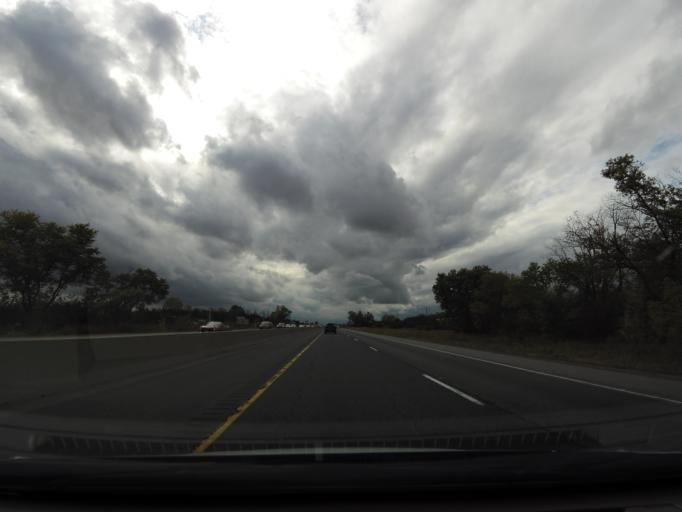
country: CA
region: Ontario
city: Belleville
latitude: 44.1882
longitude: -77.4134
